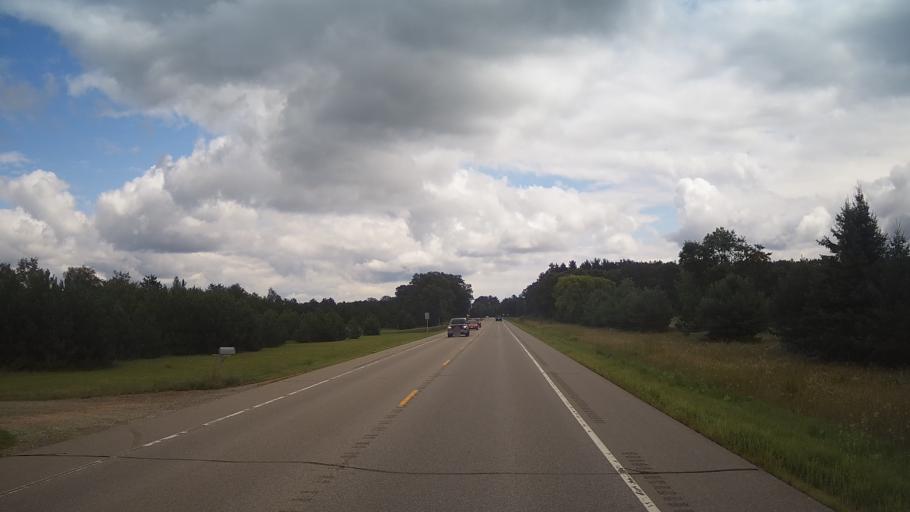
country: US
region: Wisconsin
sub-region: Adams County
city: Friendship
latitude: 44.0230
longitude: -89.6666
